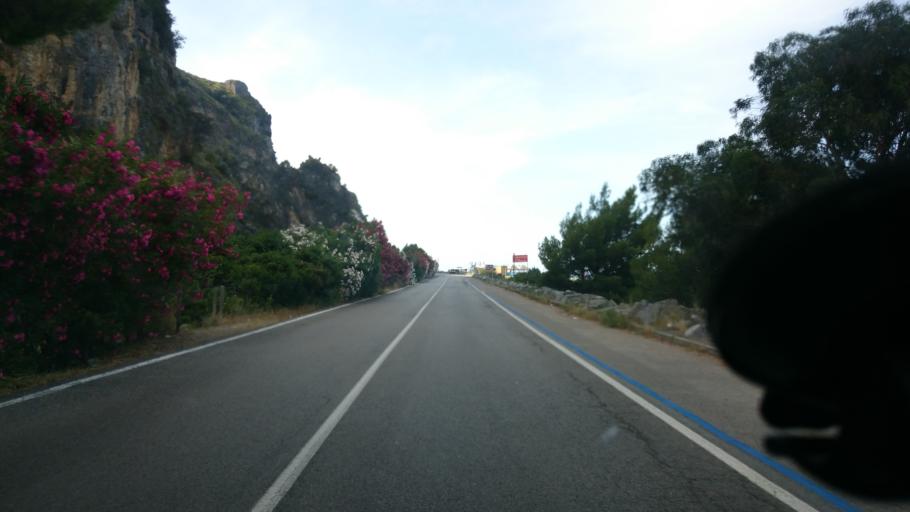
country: IT
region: Campania
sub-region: Provincia di Salerno
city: Marina di Camerota
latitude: 40.0178
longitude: 15.3326
